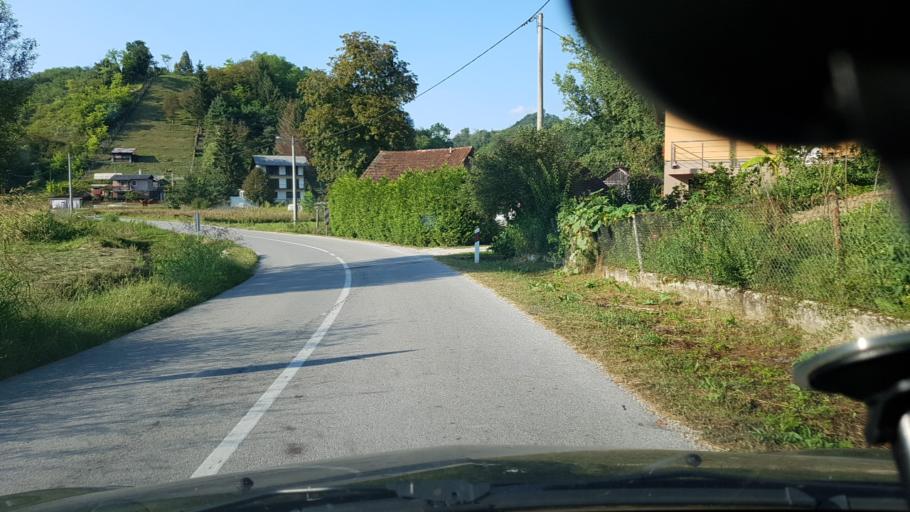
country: SI
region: Bistrica ob Sotli
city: Bistrica ob Sotli
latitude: 46.0410
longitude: 15.7736
